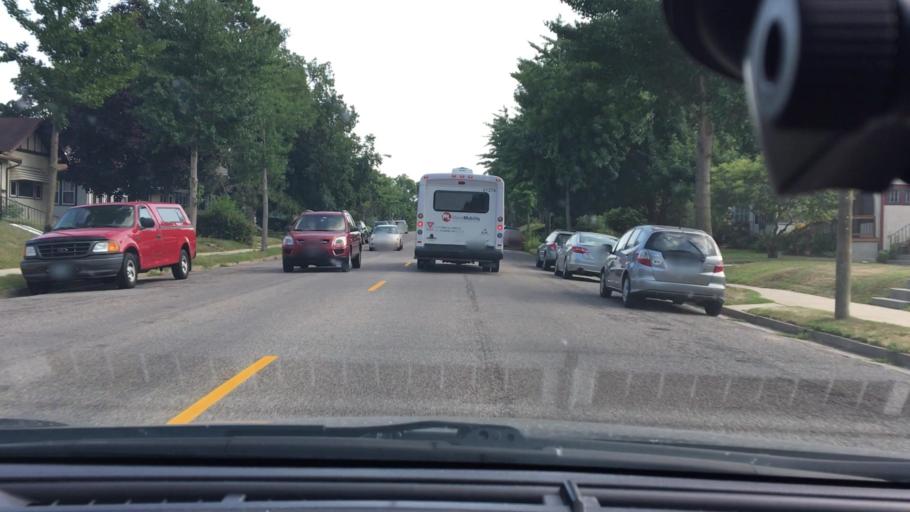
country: US
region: Minnesota
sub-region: Hennepin County
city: Richfield
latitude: 44.9173
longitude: -93.2524
